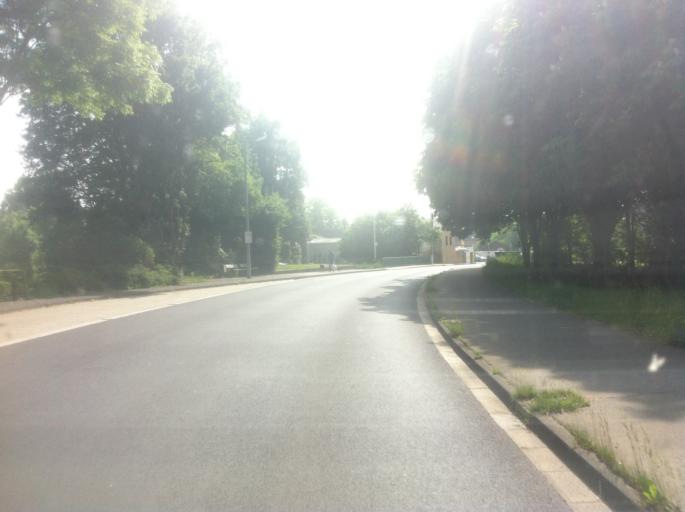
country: DE
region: North Rhine-Westphalia
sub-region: Regierungsbezirk Koln
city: Weilerswist
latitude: 50.7551
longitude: 6.7719
